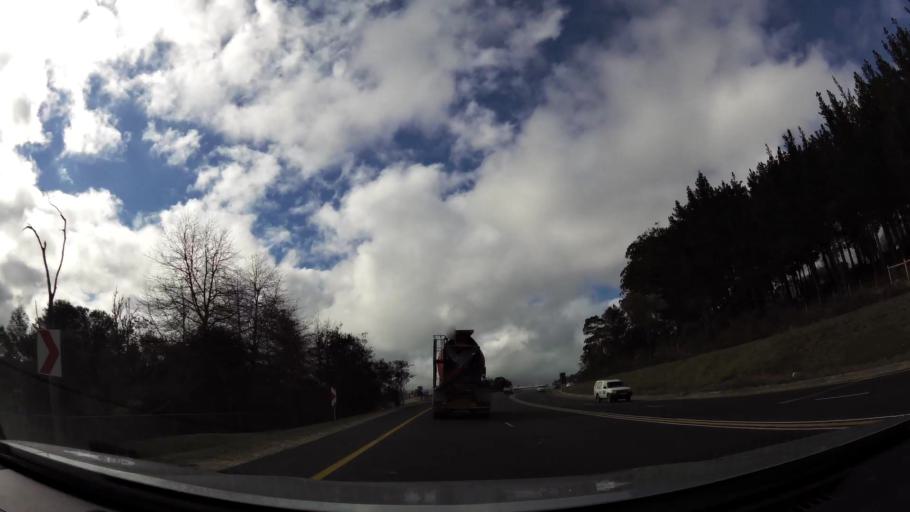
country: ZA
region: Western Cape
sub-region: Eden District Municipality
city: Knysna
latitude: -34.0418
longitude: 23.1125
